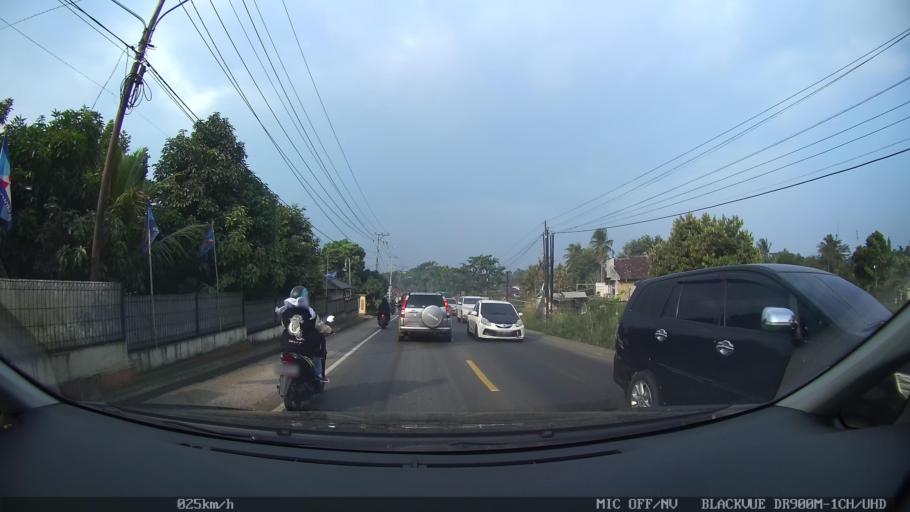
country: ID
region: Lampung
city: Natar
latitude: -5.3653
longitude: 105.1824
